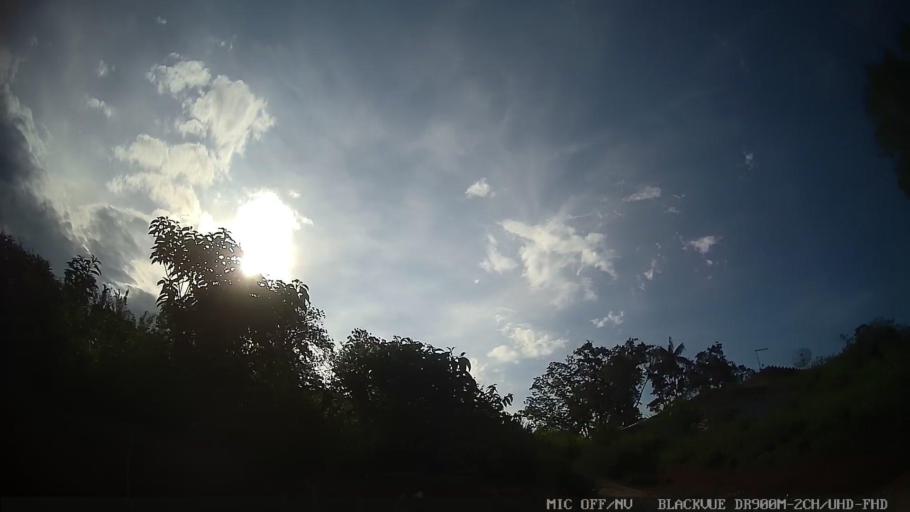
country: BR
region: Sao Paulo
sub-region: Amparo
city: Amparo
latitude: -22.6943
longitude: -46.6905
